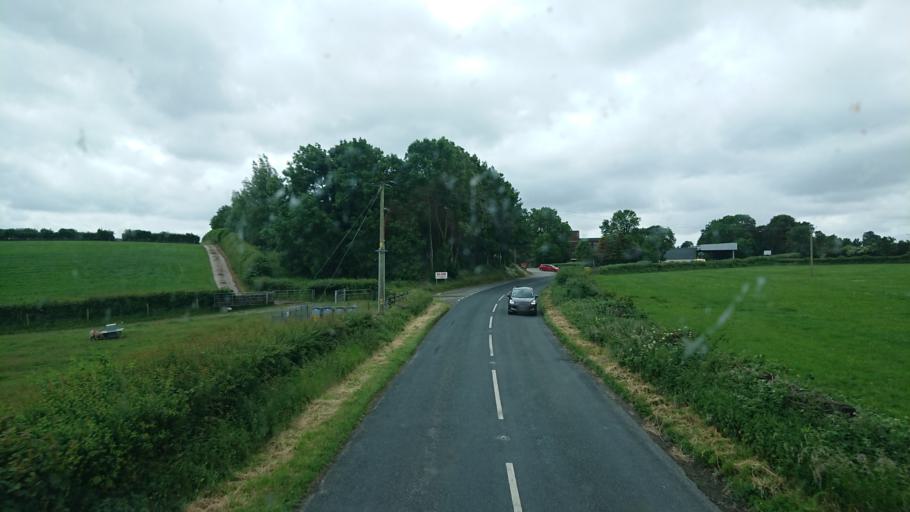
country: GB
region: England
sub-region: Cumbria
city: Milnthorpe
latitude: 54.2308
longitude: -2.7441
